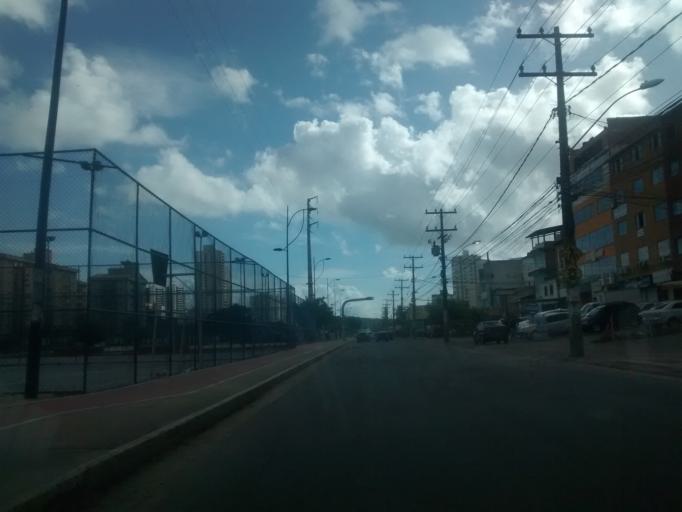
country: BR
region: Bahia
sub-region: Salvador
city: Salvador
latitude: -12.9689
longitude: -38.4302
